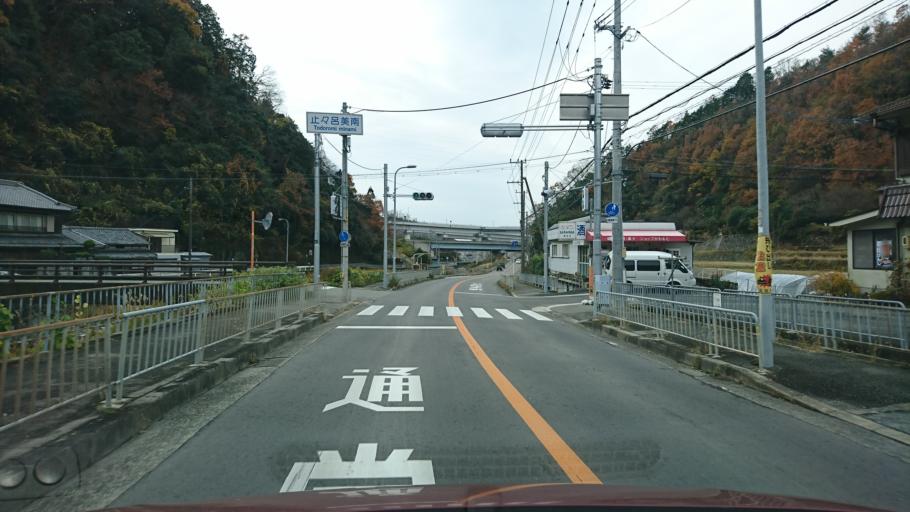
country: JP
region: Osaka
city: Mino
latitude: 34.8794
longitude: 135.4591
